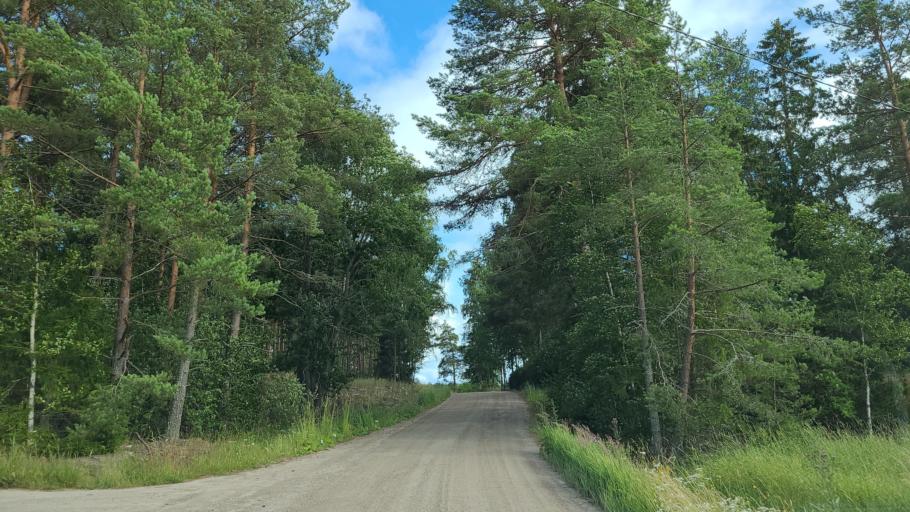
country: FI
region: Varsinais-Suomi
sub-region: Aboland-Turunmaa
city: Nagu
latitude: 60.1425
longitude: 21.7877
